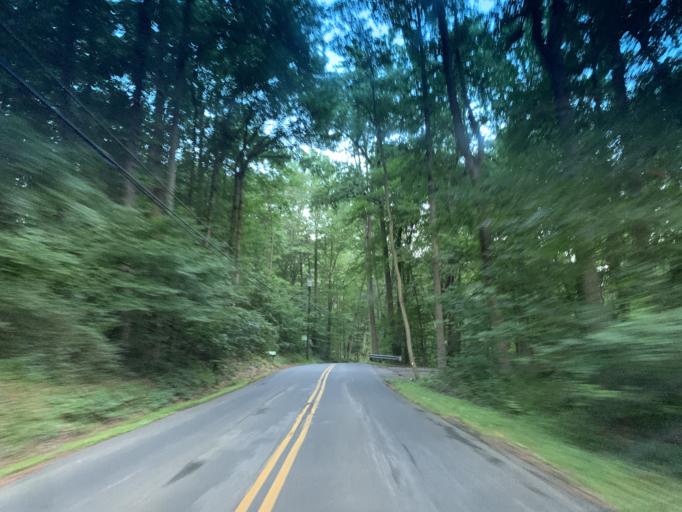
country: US
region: Maryland
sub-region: Harford County
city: Aberdeen
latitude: 39.5373
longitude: -76.1497
